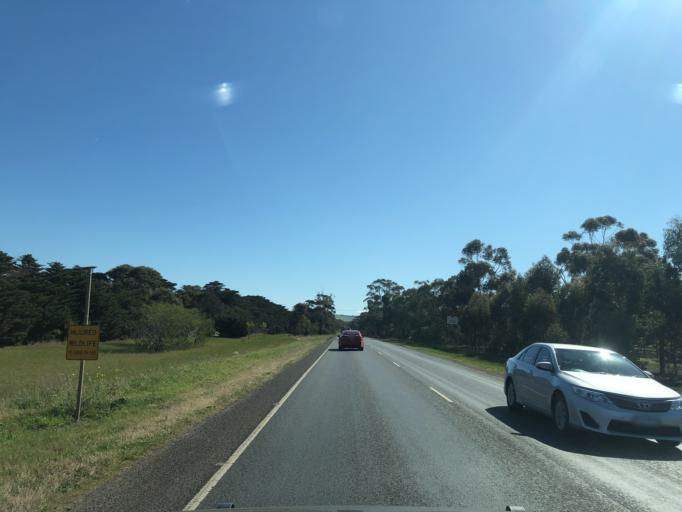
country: AU
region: Victoria
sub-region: Melton
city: Kurunjang
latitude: -37.6225
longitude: 144.6310
